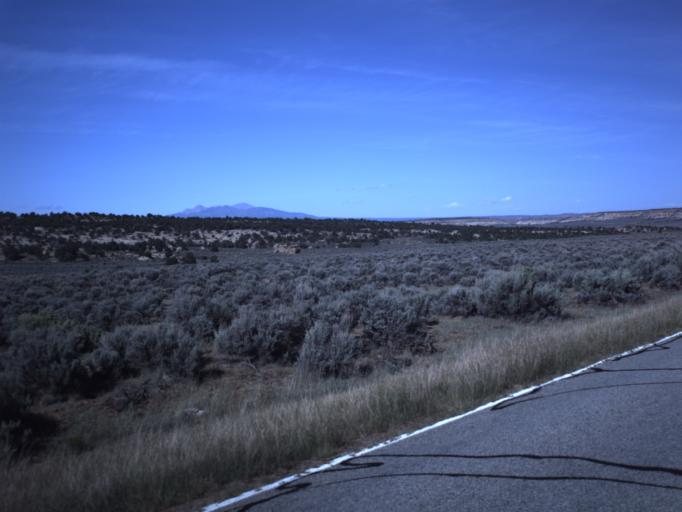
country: US
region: Utah
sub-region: San Juan County
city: Monticello
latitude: 37.9991
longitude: -109.4694
